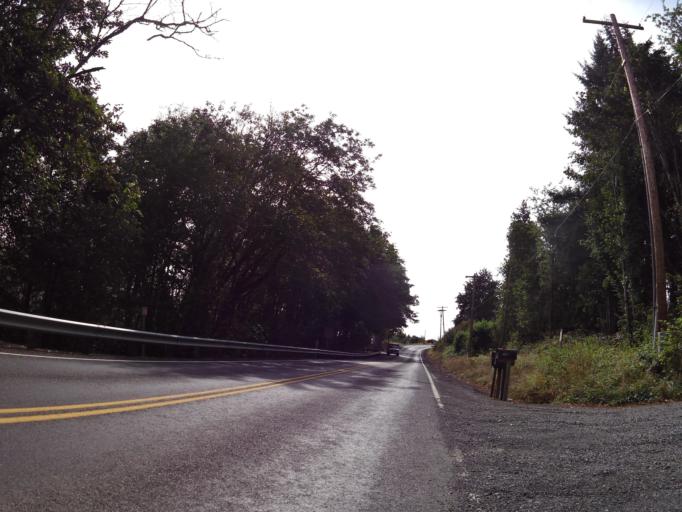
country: US
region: Washington
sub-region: Lewis County
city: Chehalis
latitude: 46.6287
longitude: -122.9680
